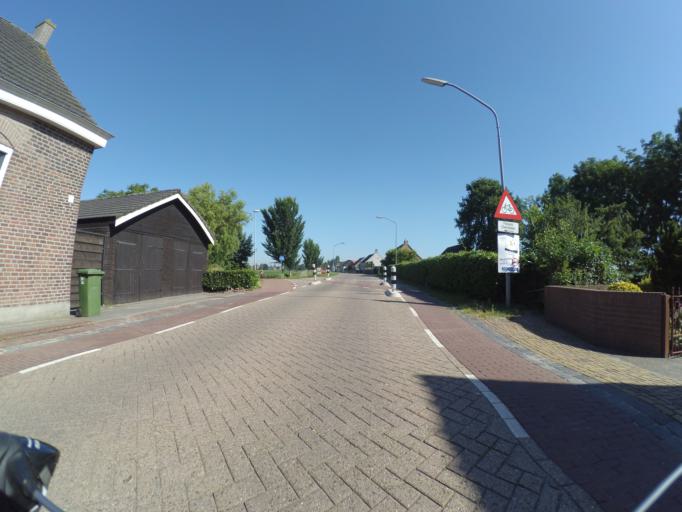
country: NL
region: North Brabant
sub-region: Gemeente Made en Drimmelen
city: Made
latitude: 51.6758
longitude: 4.7547
